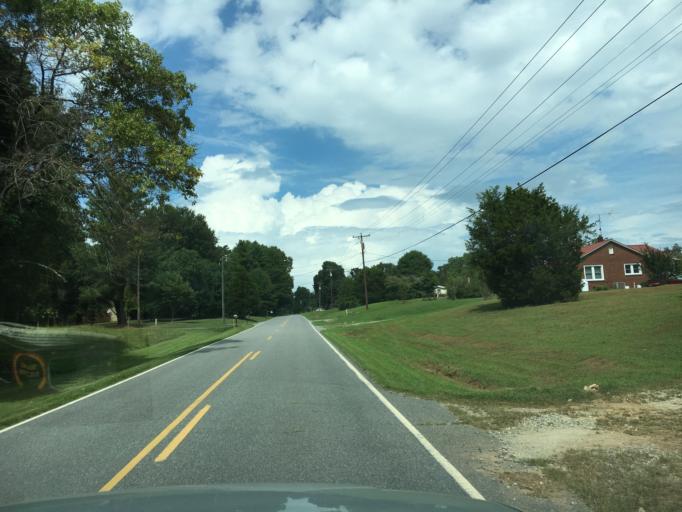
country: US
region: North Carolina
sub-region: Catawba County
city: Maiden
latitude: 35.5883
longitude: -81.1919
